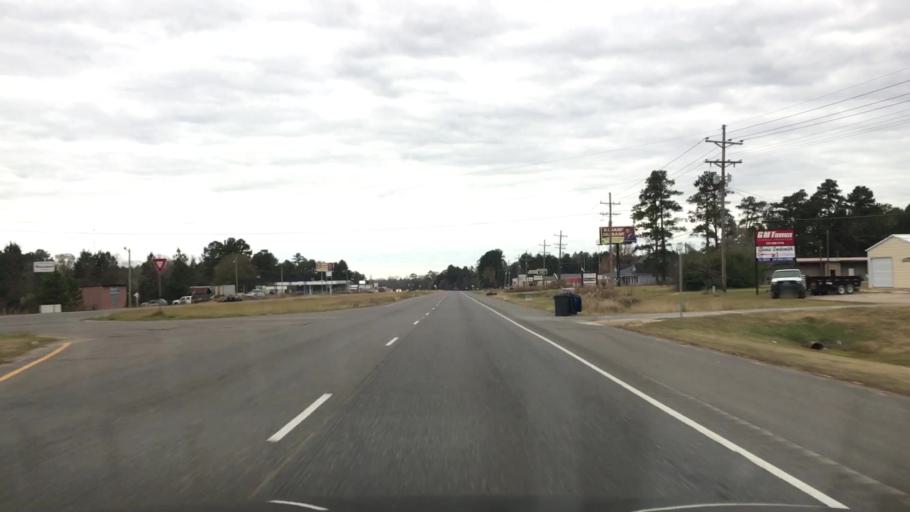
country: US
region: Louisiana
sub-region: Vernon Parish
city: New Llano
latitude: 31.0768
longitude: -93.2732
